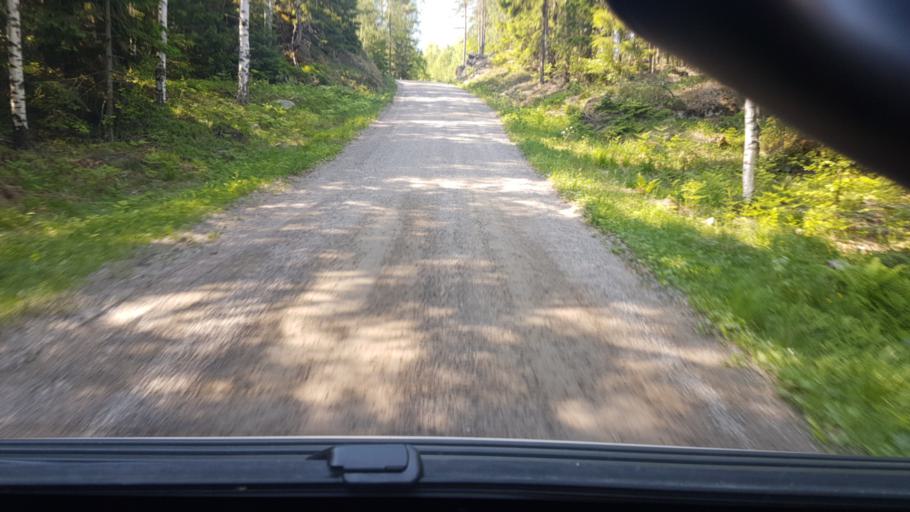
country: SE
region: Vaermland
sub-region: Eda Kommun
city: Amotfors
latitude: 59.8261
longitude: 12.4030
